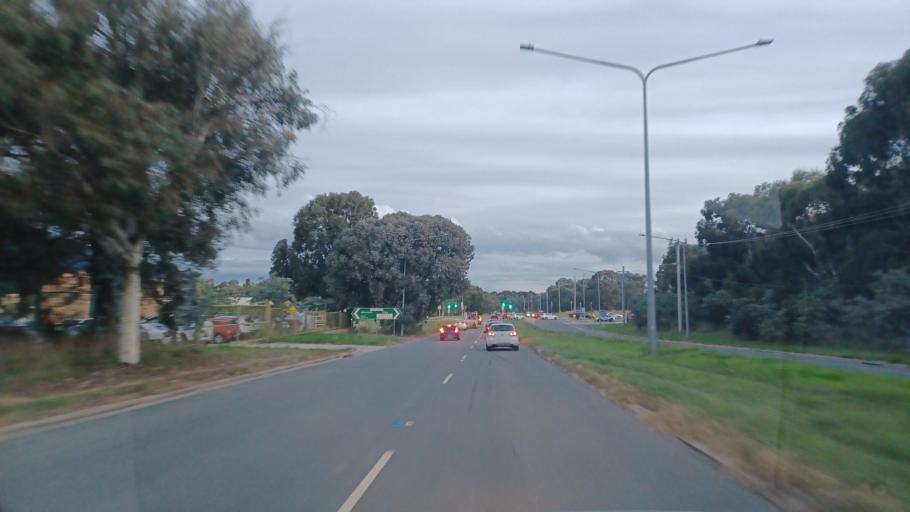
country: AU
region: Australian Capital Territory
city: Kaleen
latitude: -35.2187
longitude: 149.1369
